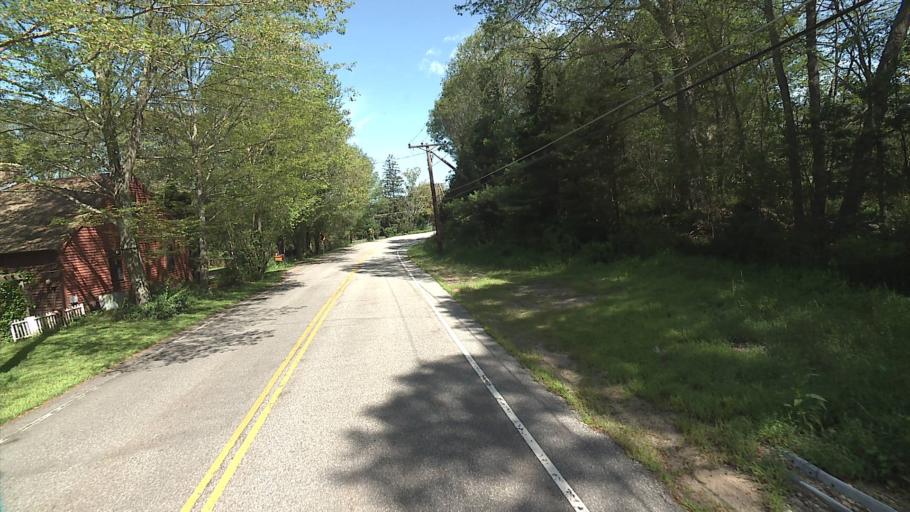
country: US
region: Connecticut
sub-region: New London County
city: Baltic
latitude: 41.6848
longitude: -72.0858
